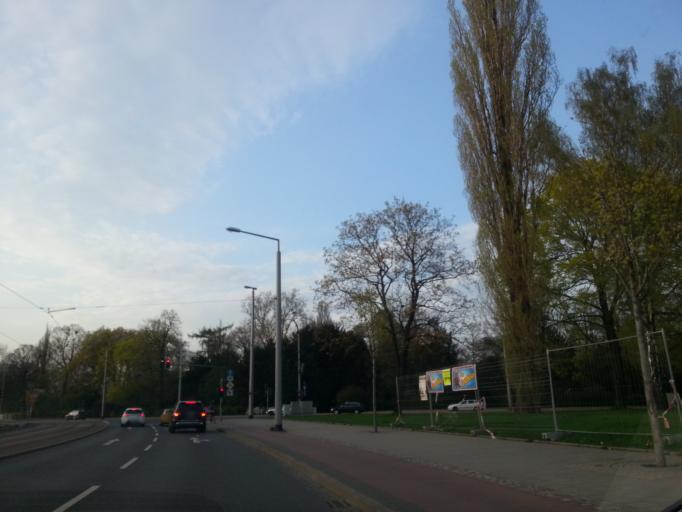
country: DE
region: Saxony
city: Dresden
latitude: 51.0368
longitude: 13.7494
